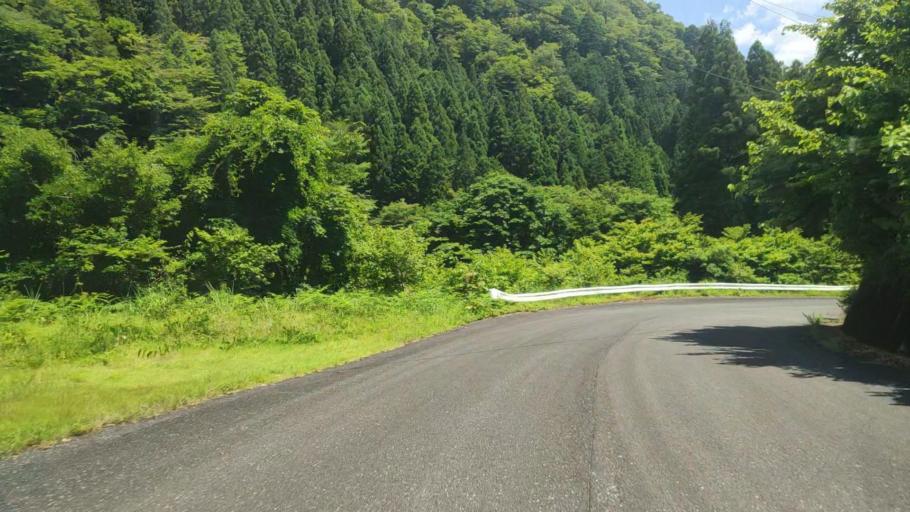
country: JP
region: Fukui
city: Ono
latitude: 35.7344
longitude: 136.5797
